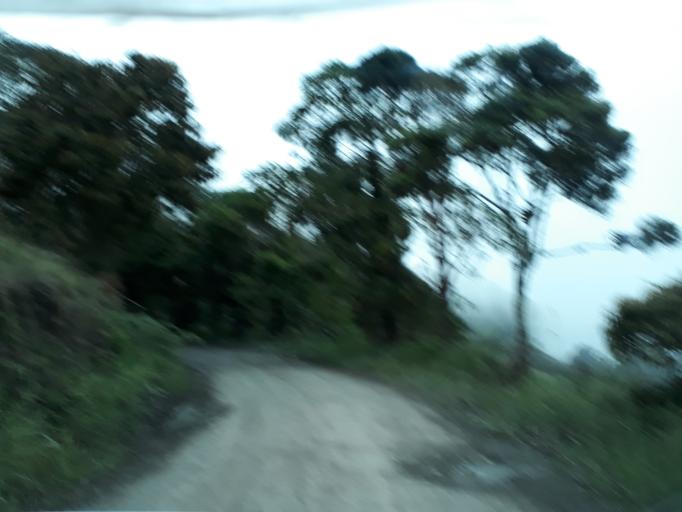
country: CO
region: Boyaca
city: Muzo
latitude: 5.3708
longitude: -74.0731
